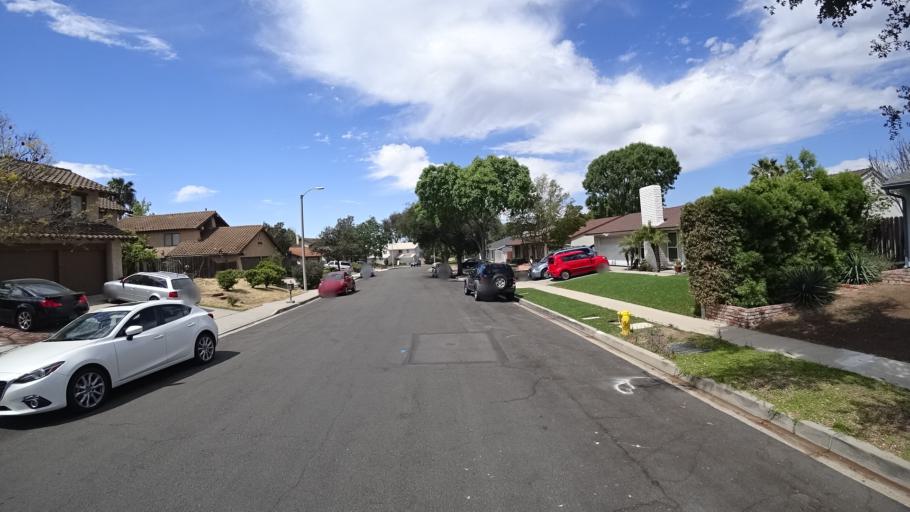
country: US
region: California
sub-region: Ventura County
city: Casa Conejo
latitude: 34.1648
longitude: -118.9412
